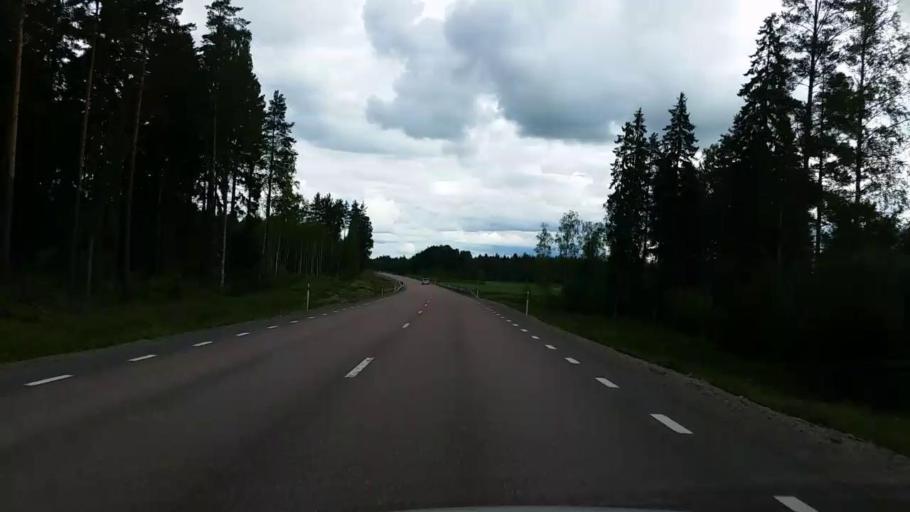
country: SE
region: Dalarna
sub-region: Avesta Kommun
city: Horndal
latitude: 60.4735
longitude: 16.4481
